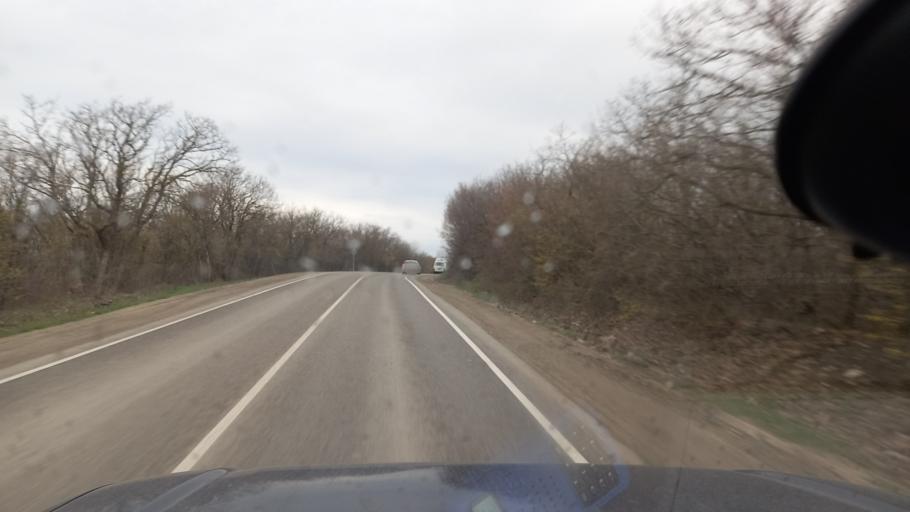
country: RU
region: Krasnodarskiy
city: Sukko
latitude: 44.8402
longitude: 37.4079
